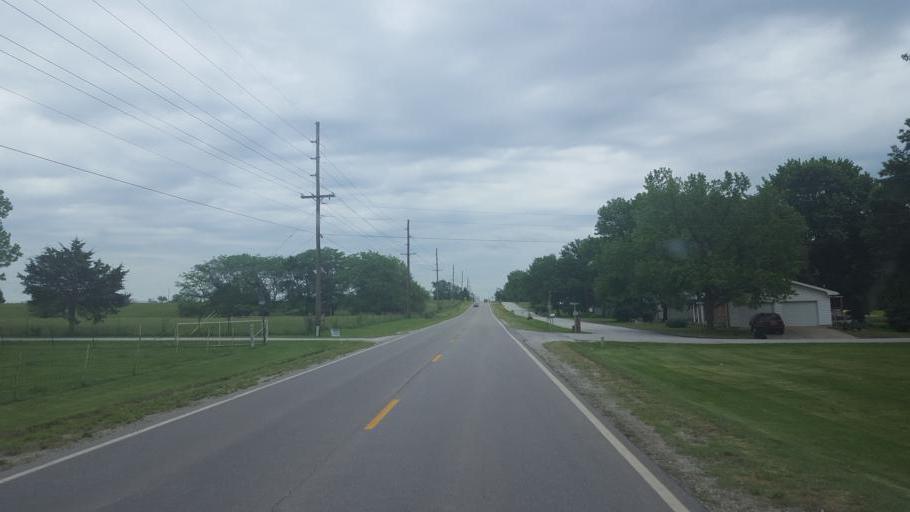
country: US
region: Missouri
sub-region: Moniteau County
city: California
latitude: 38.6359
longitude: -92.6052
